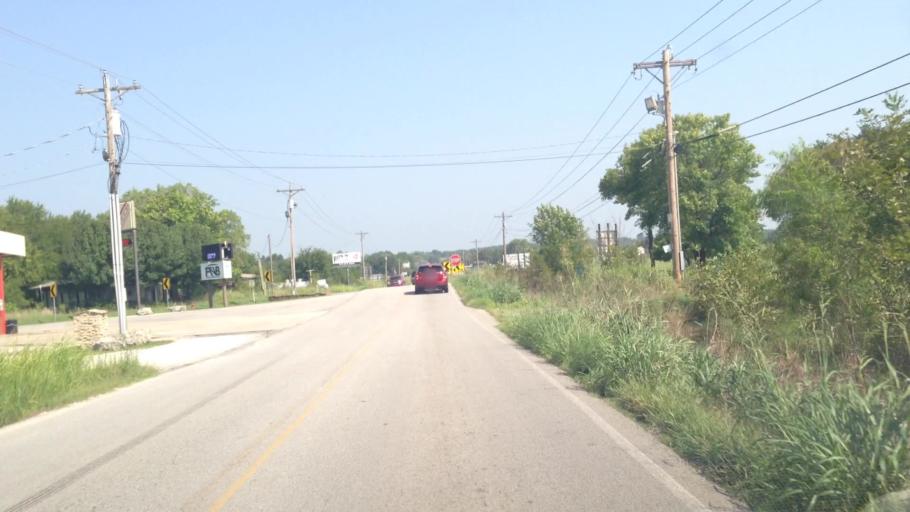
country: US
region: Oklahoma
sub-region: Delaware County
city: Cleora
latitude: 36.5715
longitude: -94.9707
